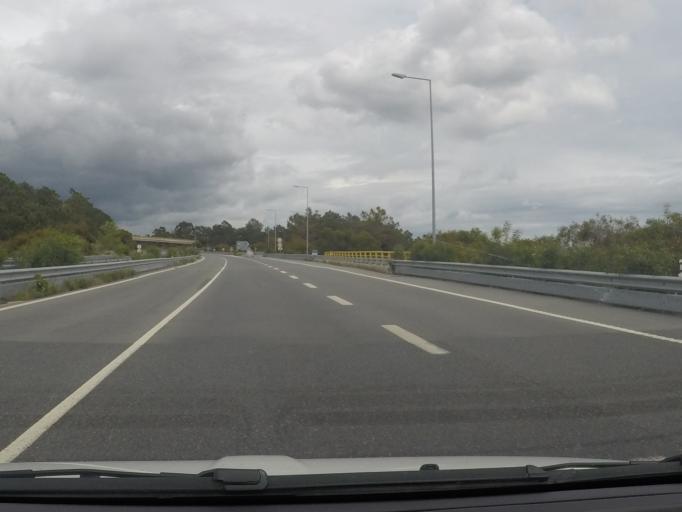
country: PT
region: Setubal
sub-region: Sines
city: Sines
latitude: 37.9735
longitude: -8.8125
